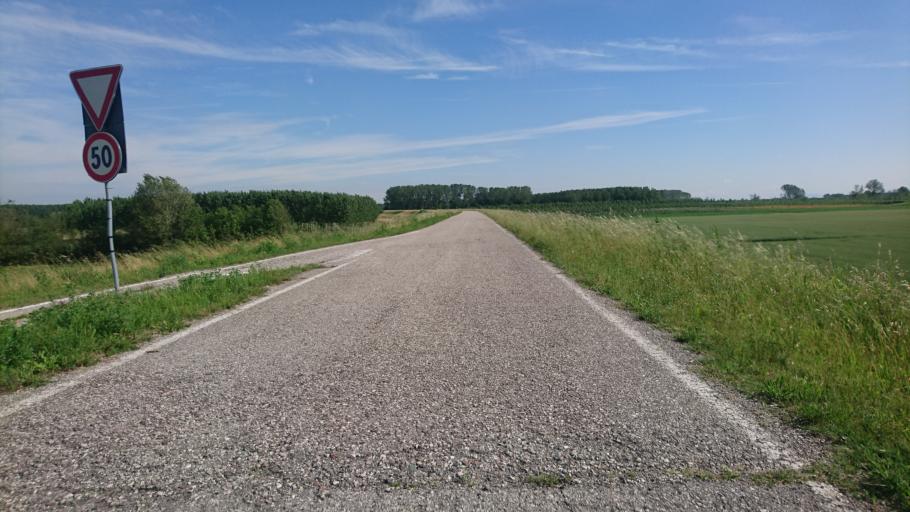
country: IT
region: Veneto
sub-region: Provincia di Rovigo
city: Bergantino
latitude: 45.0415
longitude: 11.2627
